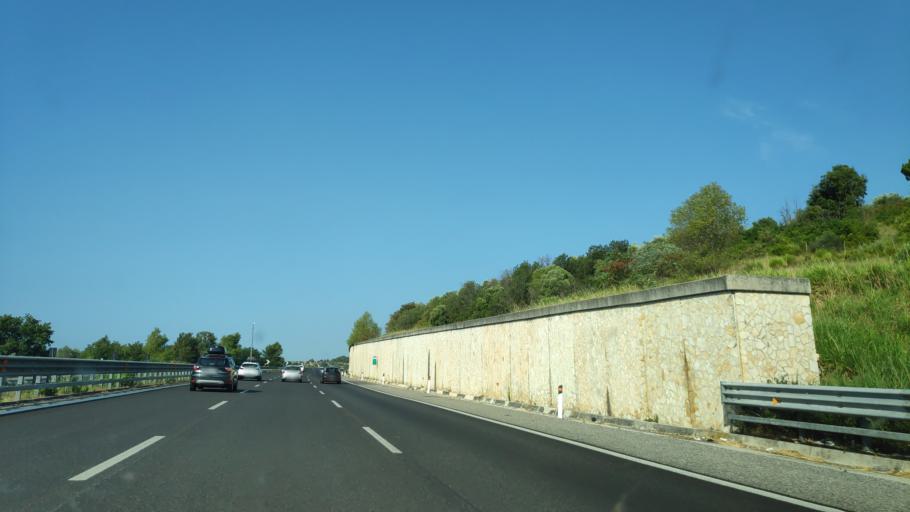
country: IT
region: Campania
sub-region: Provincia di Salerno
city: Serre
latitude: 40.6144
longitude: 15.1529
